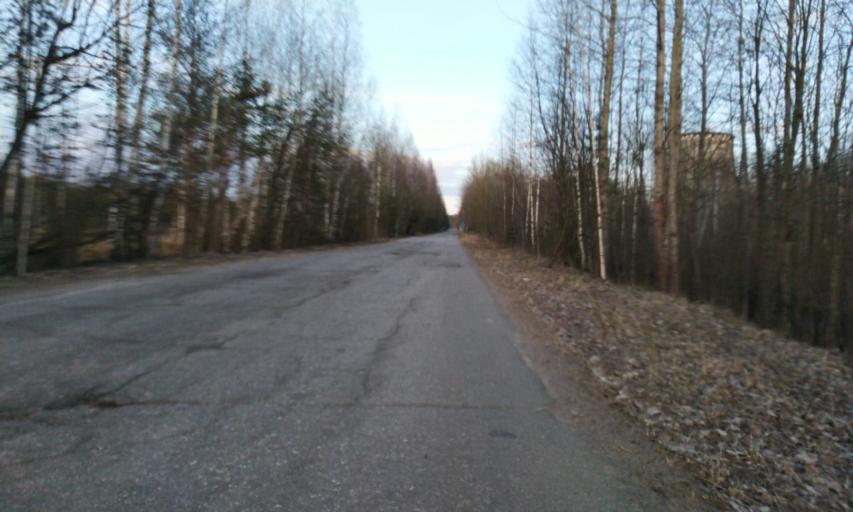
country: RU
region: Leningrad
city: Novoye Devyatkino
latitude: 60.0786
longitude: 30.4824
